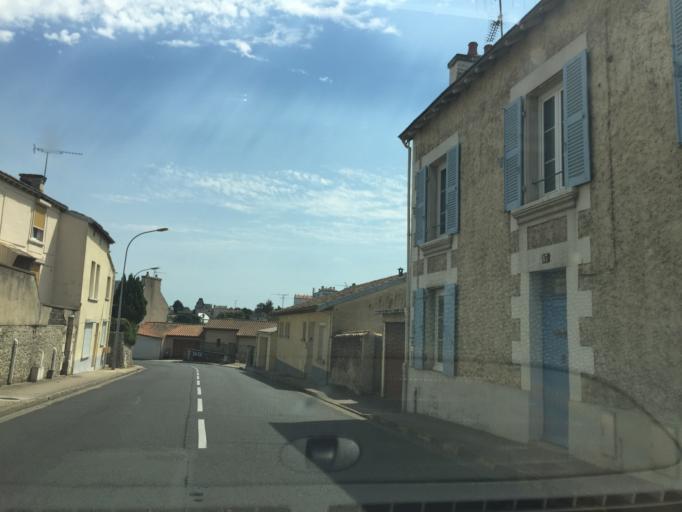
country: FR
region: Poitou-Charentes
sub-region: Departement de la Vienne
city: Poitiers
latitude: 46.5769
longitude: 0.3233
